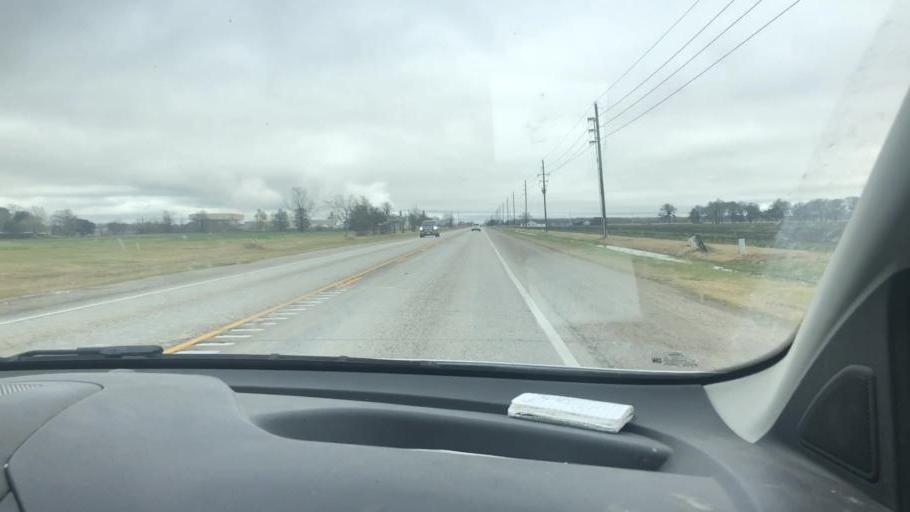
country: US
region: Texas
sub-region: Wharton County
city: Wharton
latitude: 29.3025
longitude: -96.0795
